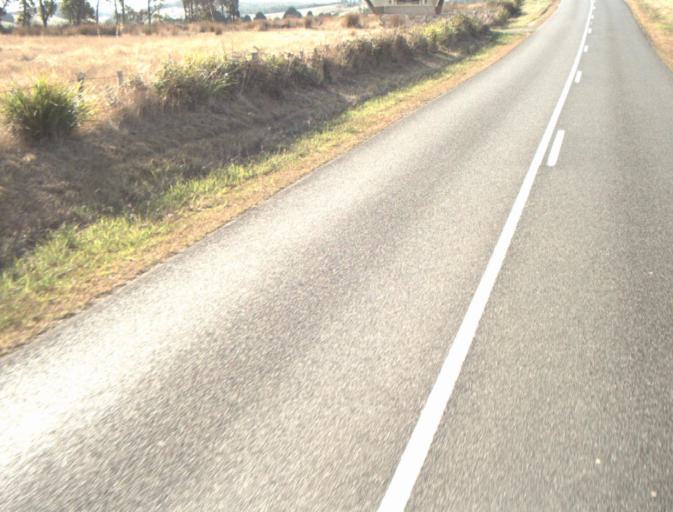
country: AU
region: Tasmania
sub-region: Launceston
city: Mayfield
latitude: -41.2173
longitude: 147.1216
